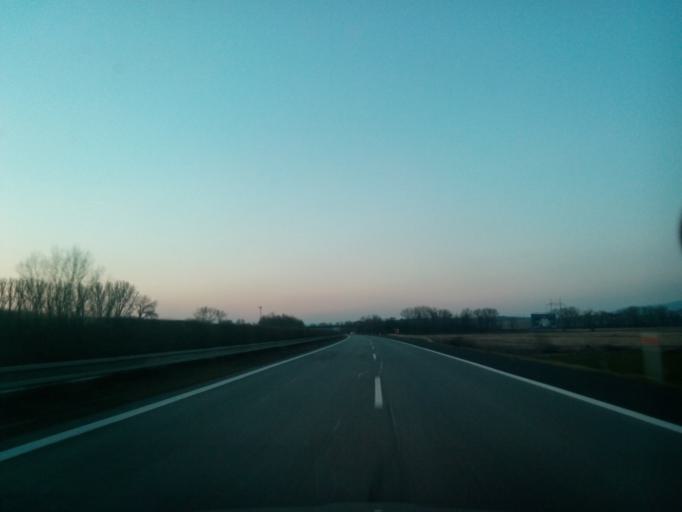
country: SK
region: Kosicky
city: Kosice
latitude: 48.8262
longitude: 21.3093
